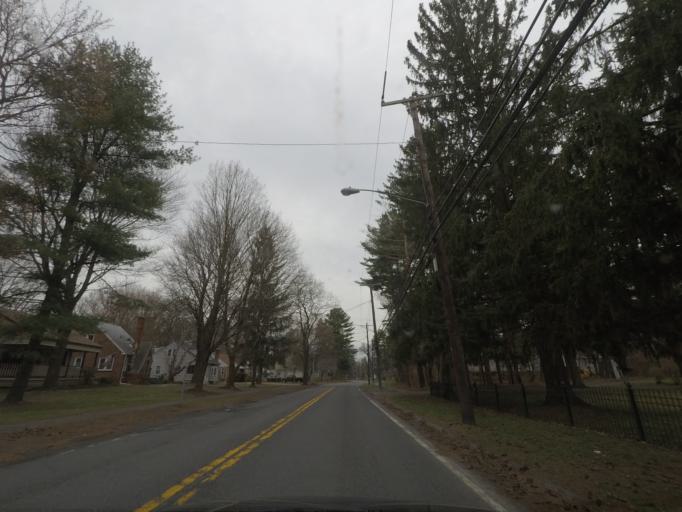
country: US
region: New York
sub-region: Albany County
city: Delmar
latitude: 42.6200
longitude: -73.8203
